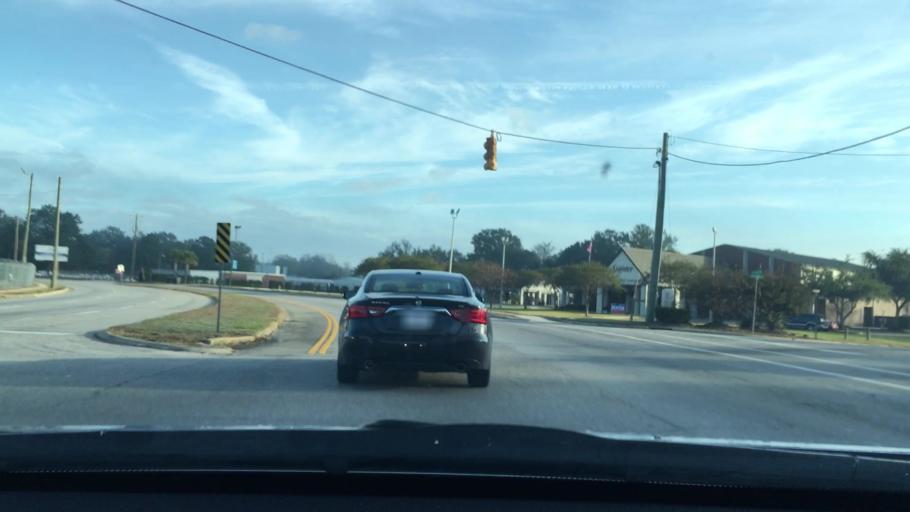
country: US
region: South Carolina
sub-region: Sumter County
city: South Sumter
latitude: 33.8969
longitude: -80.3371
